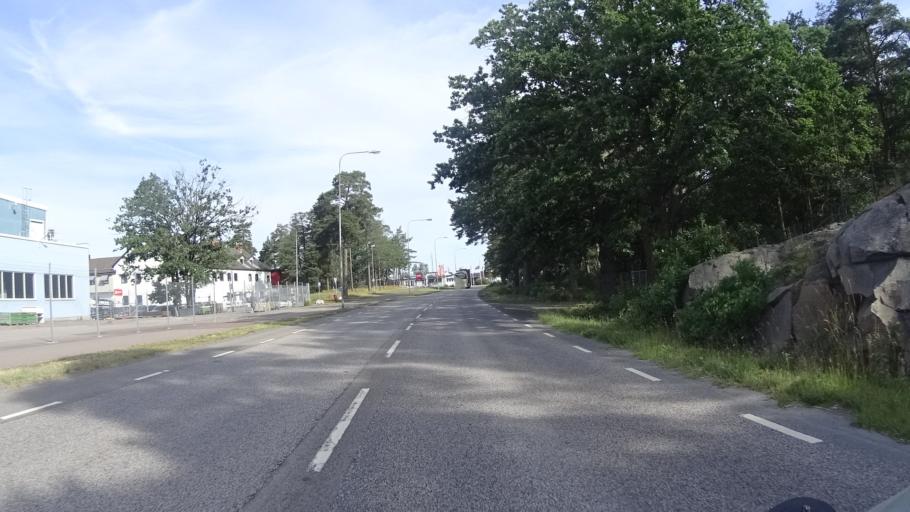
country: SE
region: Kalmar
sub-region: Oskarshamns Kommun
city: Oskarshamn
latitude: 57.2581
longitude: 16.4326
